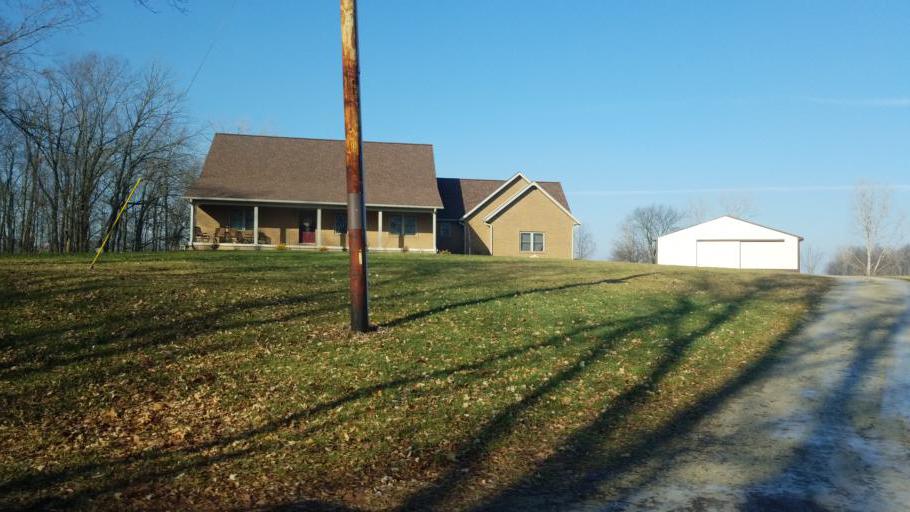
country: US
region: Ohio
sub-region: Seneca County
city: Tiffin
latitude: 41.0373
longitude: -83.0779
